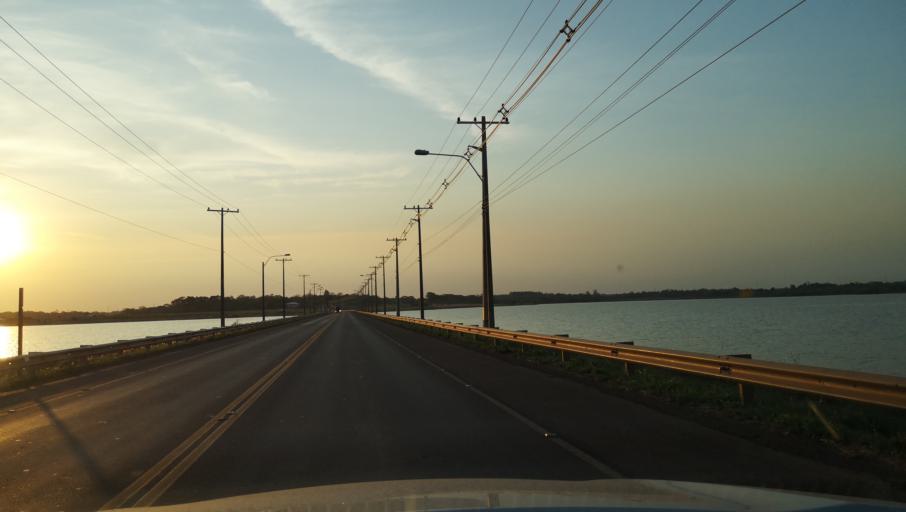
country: PY
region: Itapua
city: Carmen del Parana
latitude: -27.2044
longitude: -56.1714
